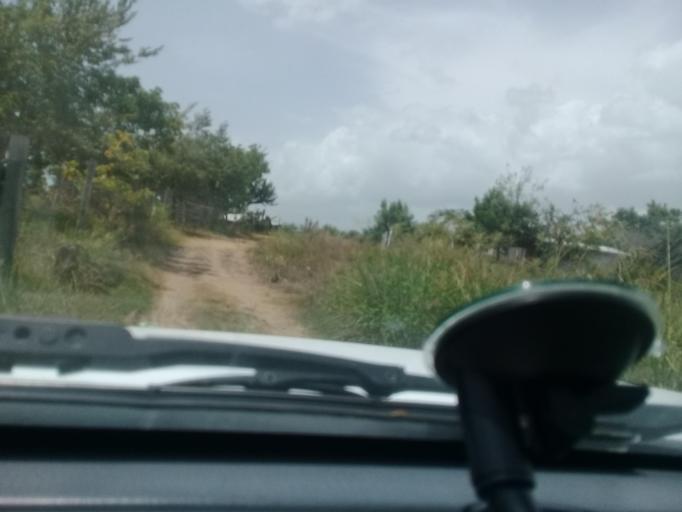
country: MX
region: Veracruz
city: Anahuac
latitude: 22.2272
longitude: -97.8260
